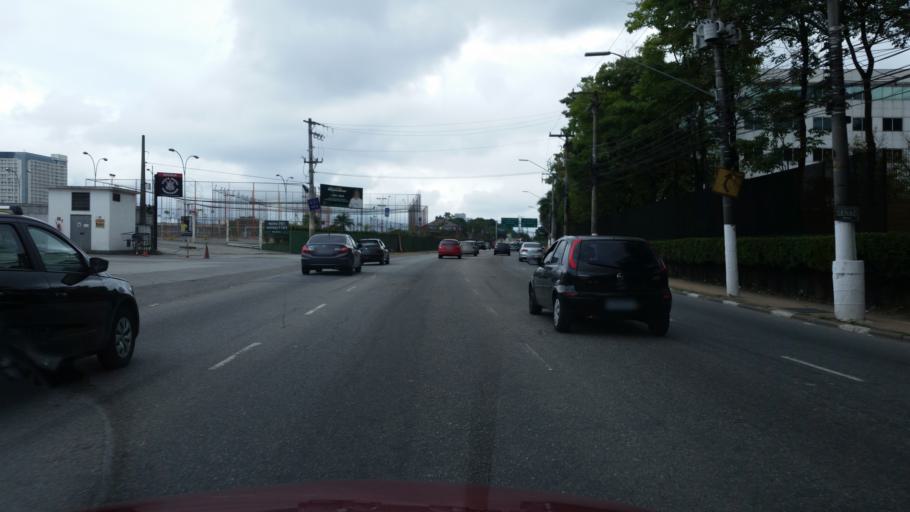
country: BR
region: Sao Paulo
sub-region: Taboao Da Serra
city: Taboao da Serra
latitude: -23.6501
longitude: -46.7266
